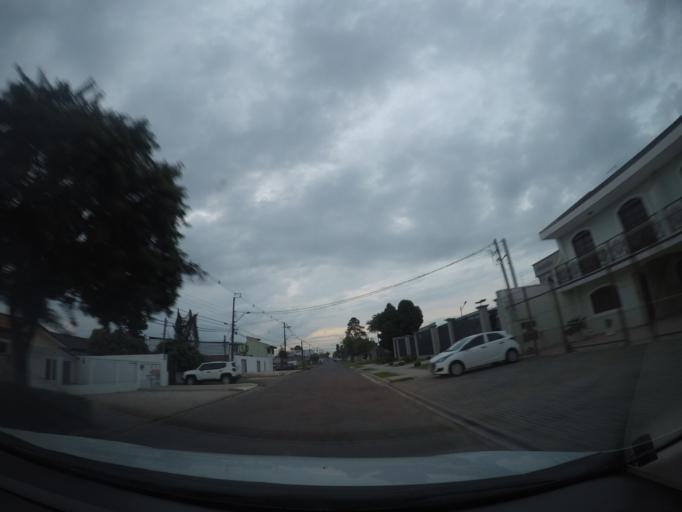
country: BR
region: Parana
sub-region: Sao Jose Dos Pinhais
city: Sao Jose dos Pinhais
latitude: -25.5140
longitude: -49.2231
